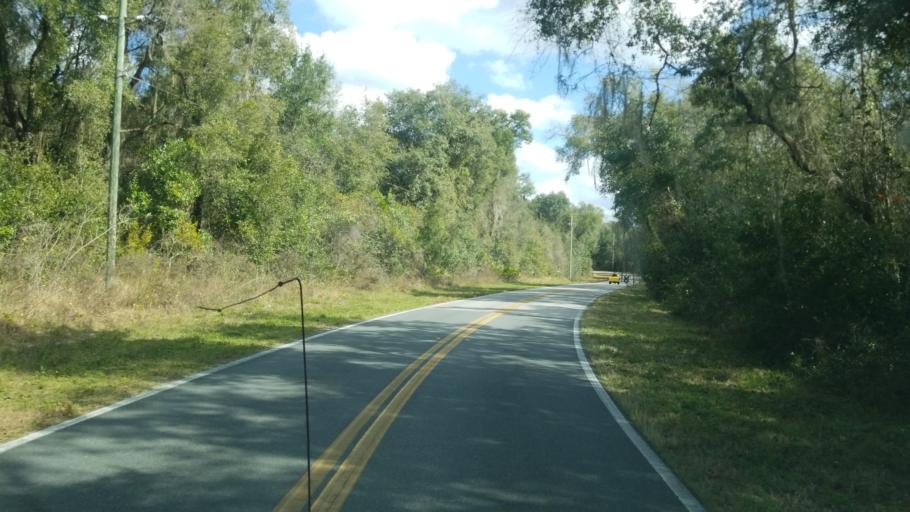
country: US
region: Florida
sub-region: Citrus County
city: Floral City
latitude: 28.7614
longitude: -82.2426
